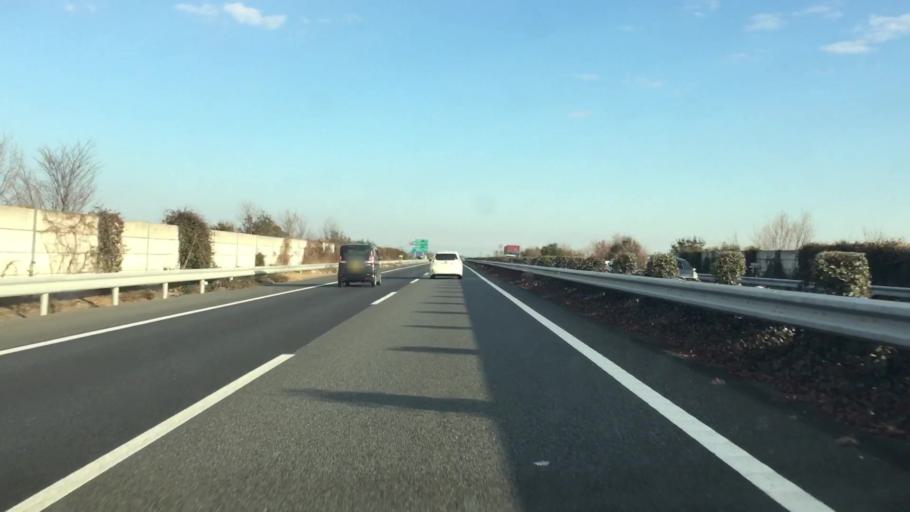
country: JP
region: Gunma
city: Isesaki
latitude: 36.3527
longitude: 139.2288
